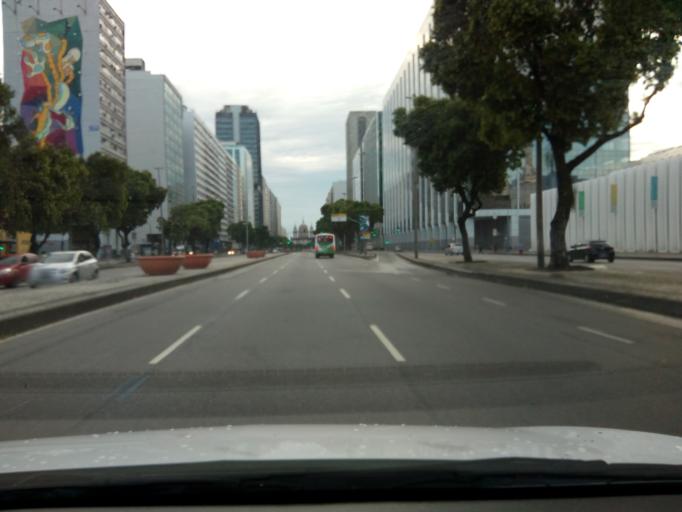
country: BR
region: Rio de Janeiro
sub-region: Rio De Janeiro
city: Rio de Janeiro
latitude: -22.9042
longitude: -43.1878
